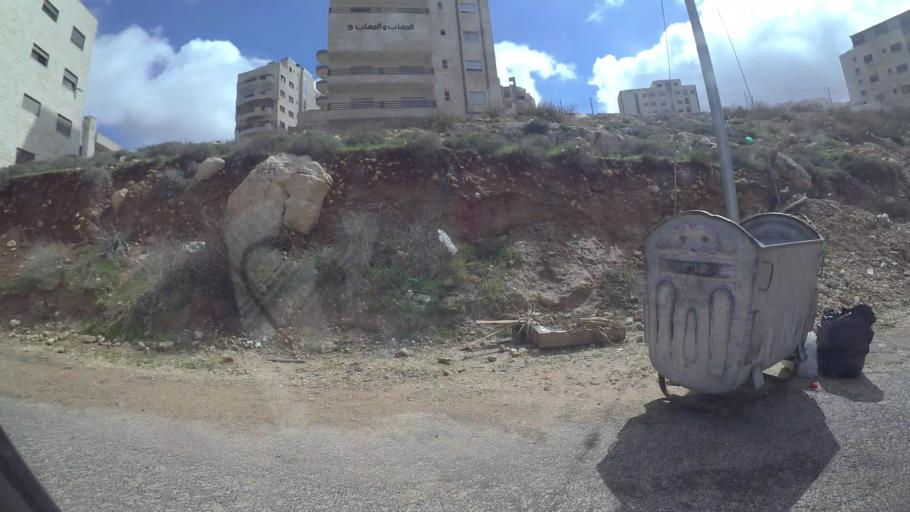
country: JO
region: Amman
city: Al Jubayhah
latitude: 32.0662
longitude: 35.8720
